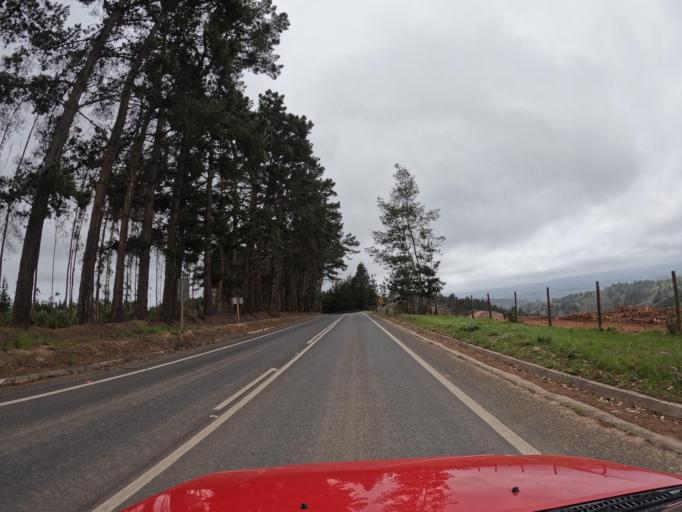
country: CL
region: O'Higgins
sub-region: Provincia de Colchagua
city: Santa Cruz
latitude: -34.5682
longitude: -72.0149
